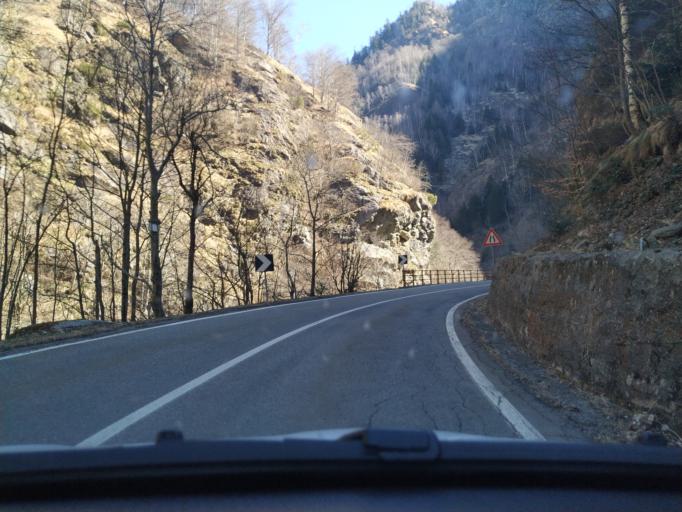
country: IT
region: Piedmont
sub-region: Provincia di Vercelli
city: Rimella
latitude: 45.8955
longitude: 8.1781
